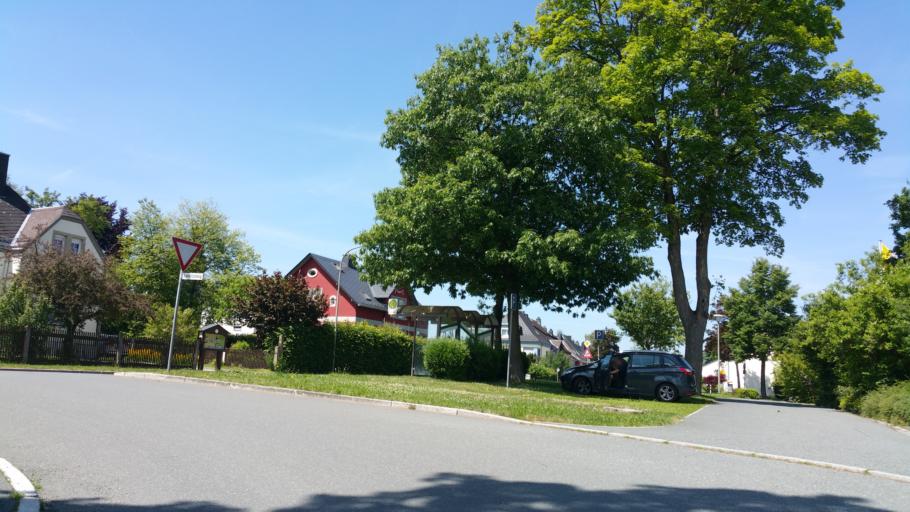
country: DE
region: Bavaria
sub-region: Upper Franconia
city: Schwarzenbach an der Saale
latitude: 50.2170
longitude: 11.9480
